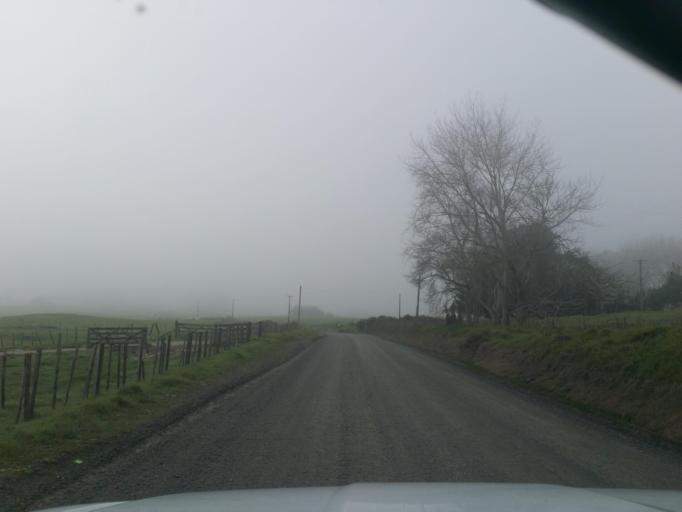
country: NZ
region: Northland
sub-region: Kaipara District
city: Dargaville
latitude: -35.9079
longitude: 173.7943
